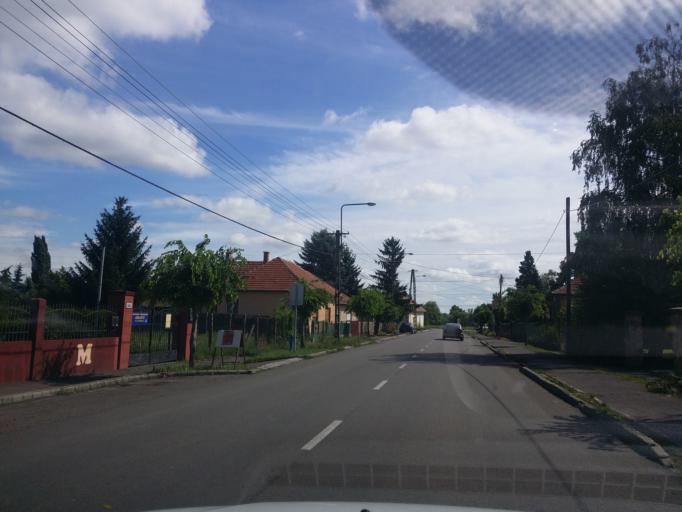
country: HU
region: Heves
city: Heves
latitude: 47.5983
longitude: 20.2915
